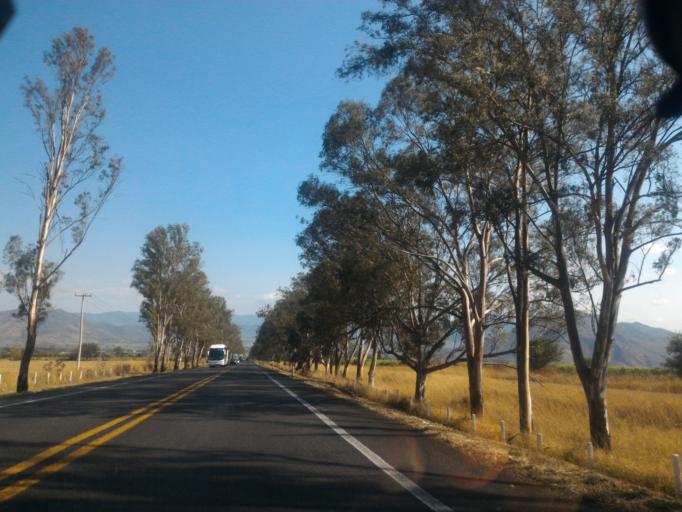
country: MX
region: Jalisco
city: Tuxpan
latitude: 19.5529
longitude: -103.4364
